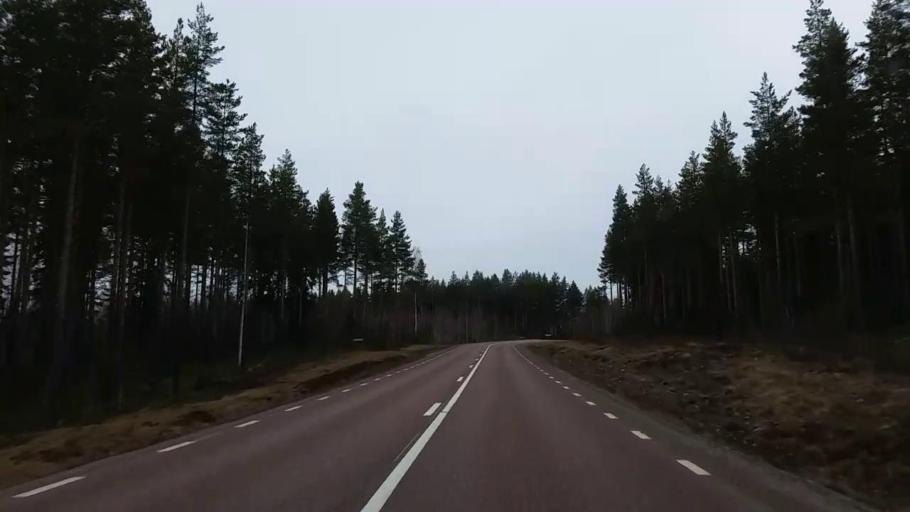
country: SE
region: Gaevleborg
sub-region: Ovanakers Kommun
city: Edsbyn
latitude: 61.2097
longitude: 15.8708
